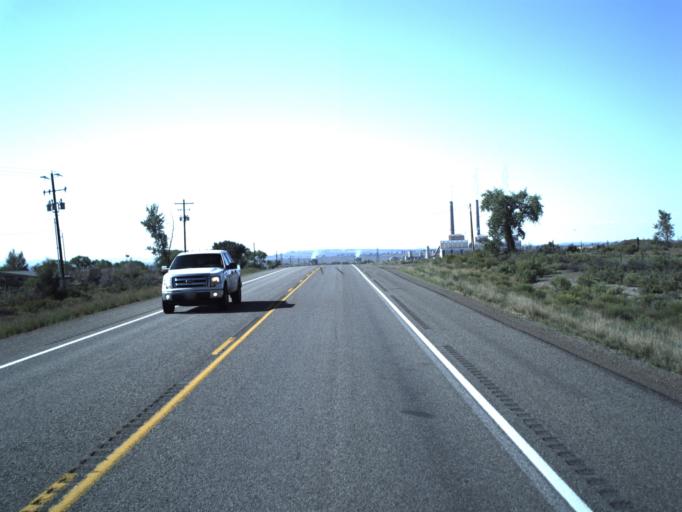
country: US
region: Utah
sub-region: Emery County
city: Castle Dale
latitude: 39.1996
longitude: -111.0242
